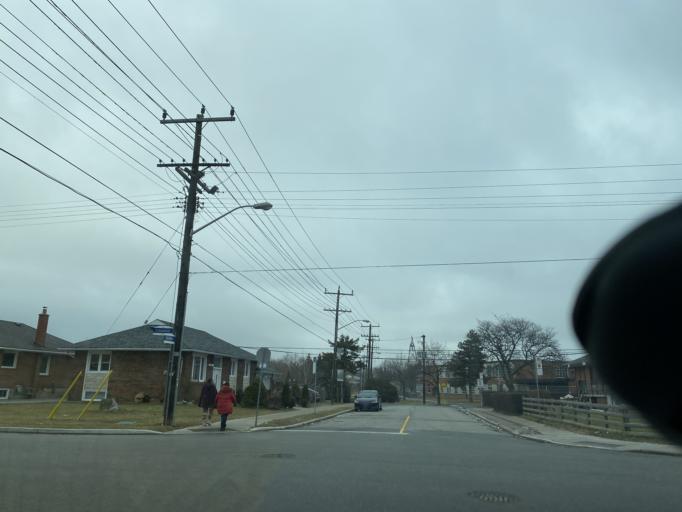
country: CA
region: Ontario
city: Scarborough
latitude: 43.7635
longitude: -79.3101
